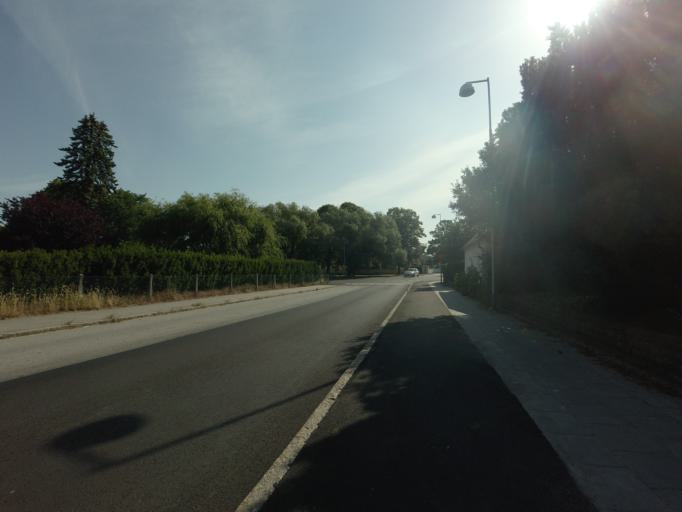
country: SE
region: Skane
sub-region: Vellinge Kommun
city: Vellinge
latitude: 55.4718
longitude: 13.0170
